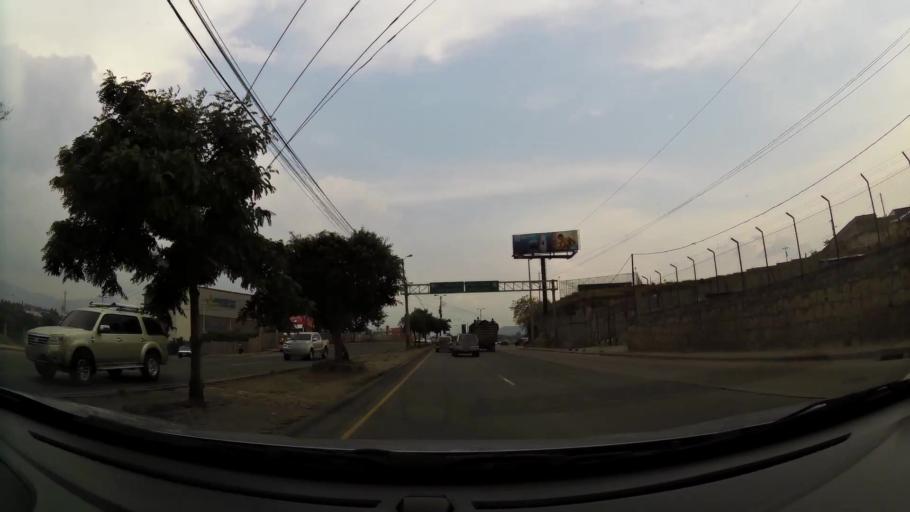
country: HN
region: Francisco Morazan
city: Tegucigalpa
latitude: 14.0760
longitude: -87.2143
